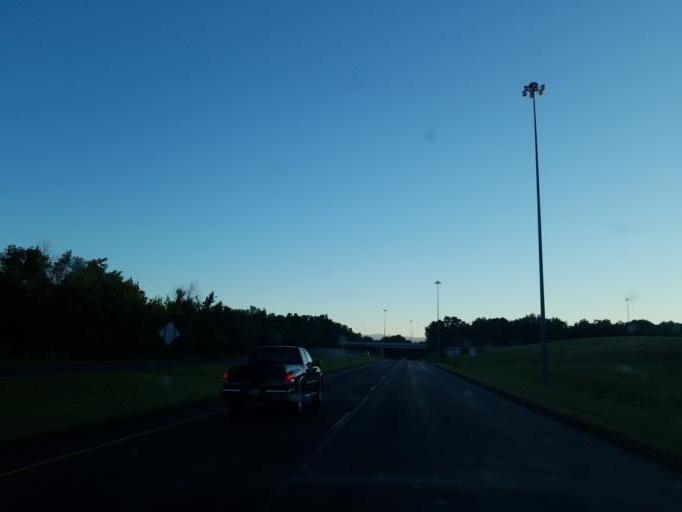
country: US
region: Ohio
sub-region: Summit County
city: Montrose-Ghent
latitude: 41.1179
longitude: -81.6542
